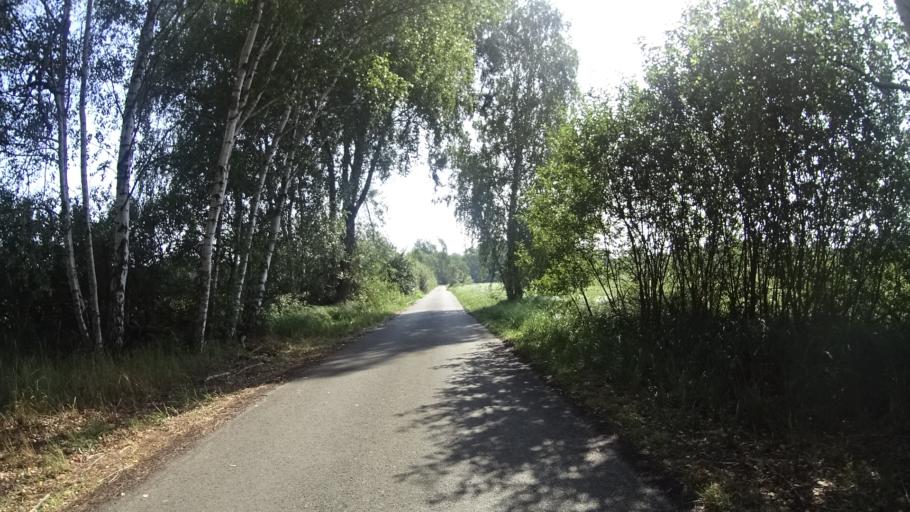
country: DE
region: Brandenburg
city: Straupitz
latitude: 51.8952
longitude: 14.1203
